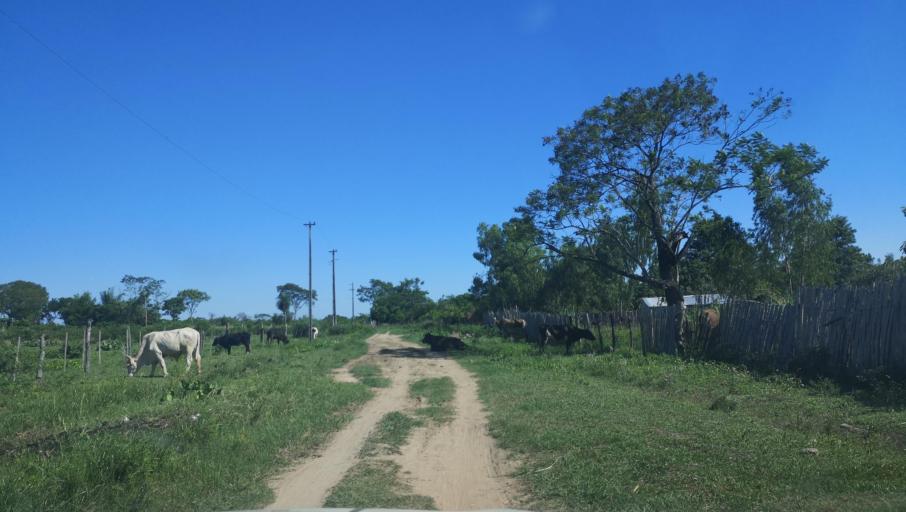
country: PY
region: Caaguazu
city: Carayao
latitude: -25.2029
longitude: -56.3951
